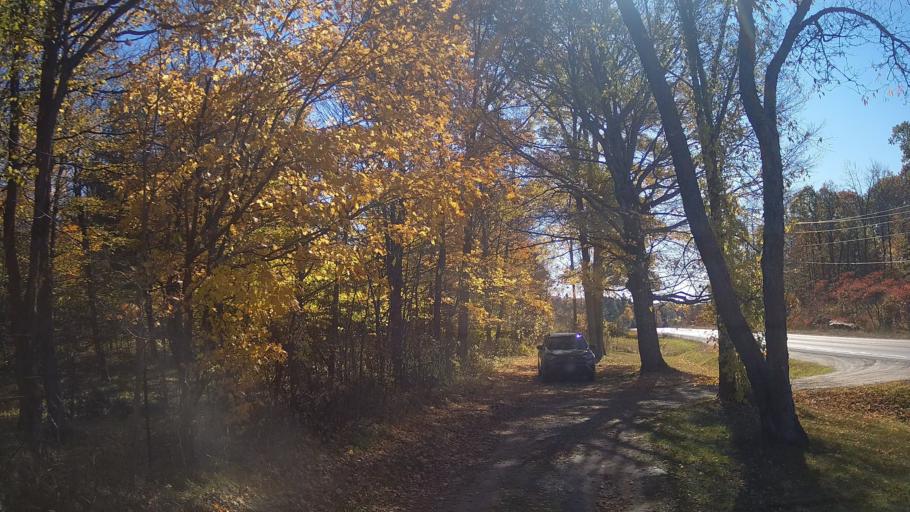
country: CA
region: Ontario
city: Kingston
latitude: 44.5566
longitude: -76.6731
